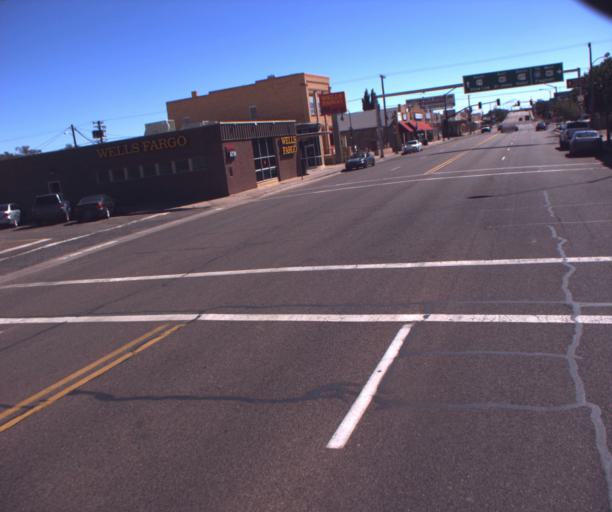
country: US
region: Arizona
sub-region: Navajo County
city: Holbrook
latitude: 34.9029
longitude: -110.1584
